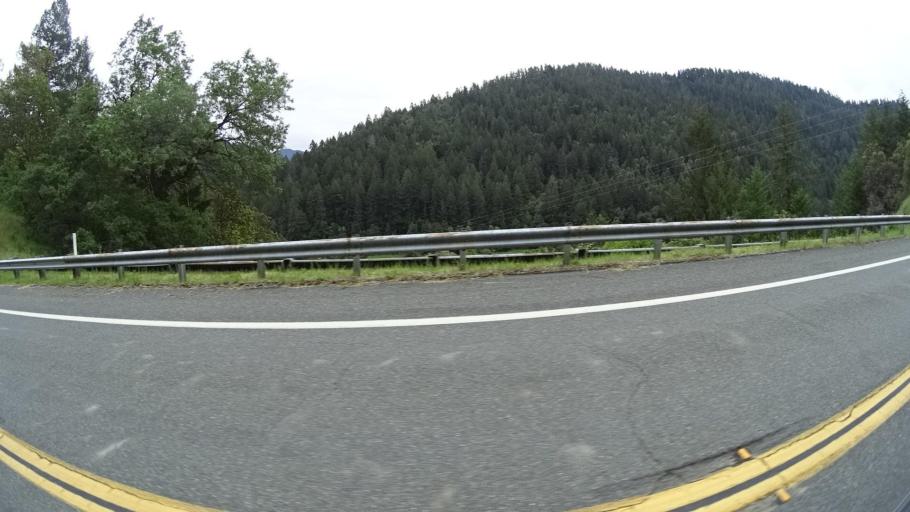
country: US
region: California
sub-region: Humboldt County
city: Willow Creek
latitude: 41.2819
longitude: -123.5823
